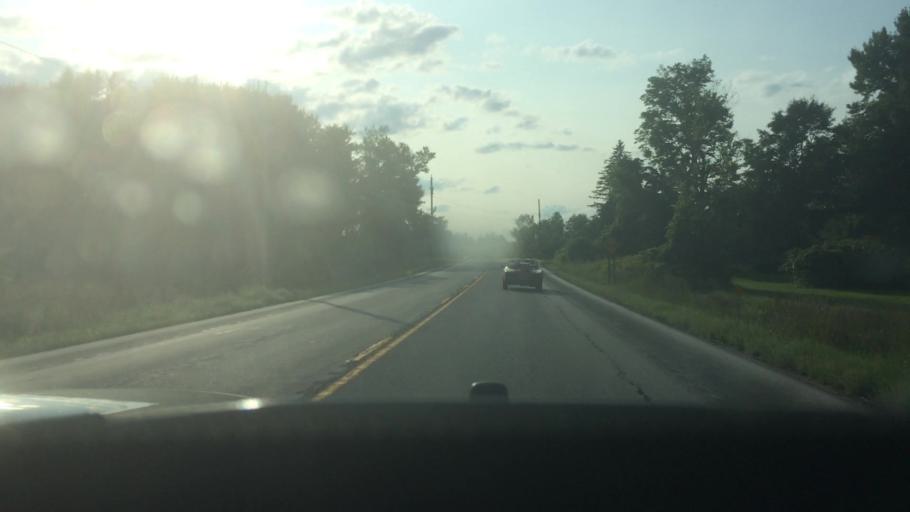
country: US
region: New York
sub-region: St. Lawrence County
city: Canton
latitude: 44.6564
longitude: -75.3189
